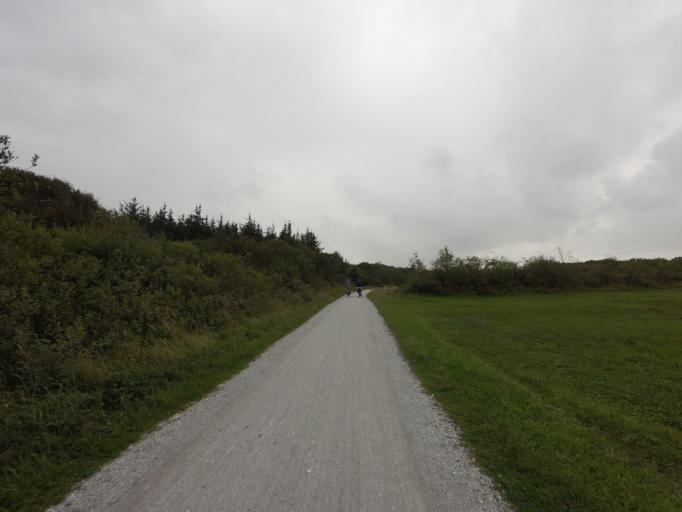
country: NL
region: Friesland
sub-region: Gemeente Schiermonnikoog
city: Schiermonnikoog
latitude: 53.4890
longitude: 6.1627
